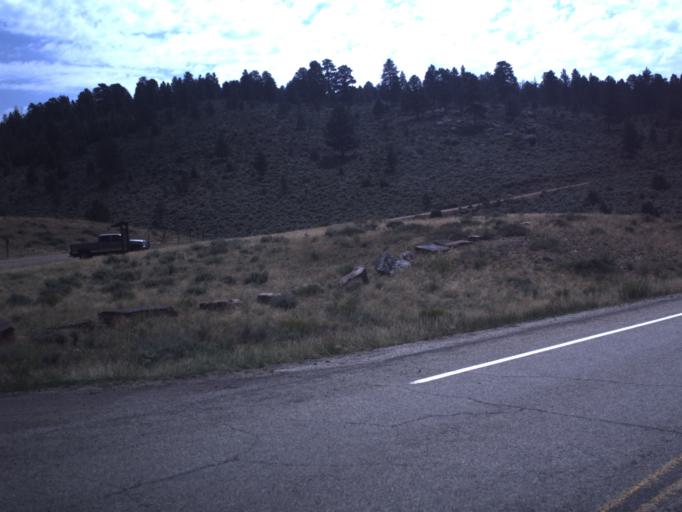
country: US
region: Utah
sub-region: Daggett County
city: Manila
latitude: 40.8822
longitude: -109.6932
